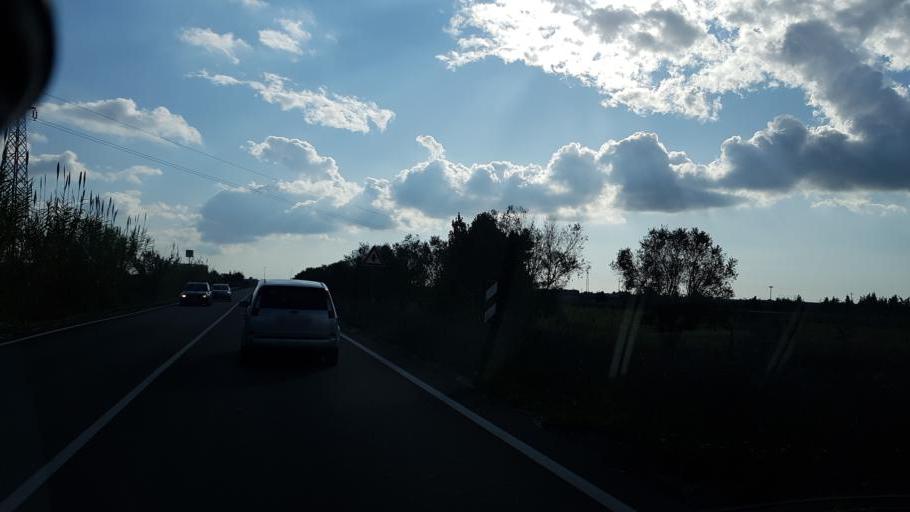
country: IT
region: Apulia
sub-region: Provincia di Lecce
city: Veglie
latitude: 40.3582
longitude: 17.9680
